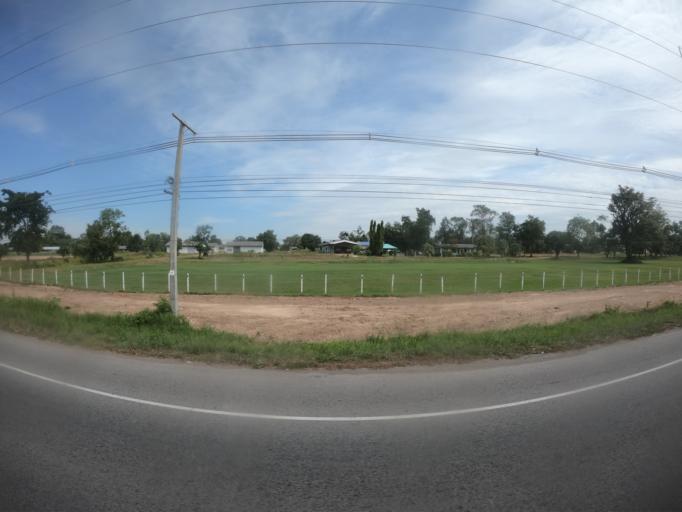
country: TH
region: Maha Sarakham
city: Chiang Yuen
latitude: 16.4322
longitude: 103.0579
